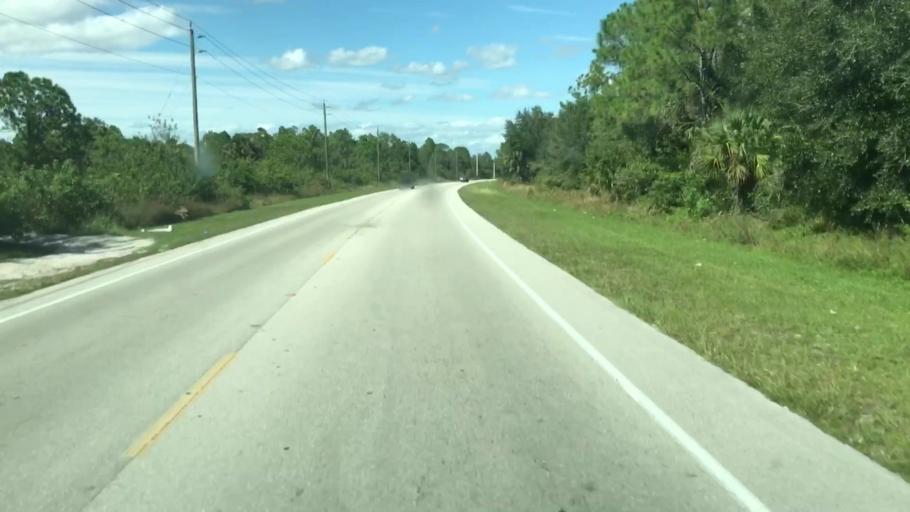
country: US
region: Florida
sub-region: Lee County
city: Alva
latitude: 26.6931
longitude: -81.6001
